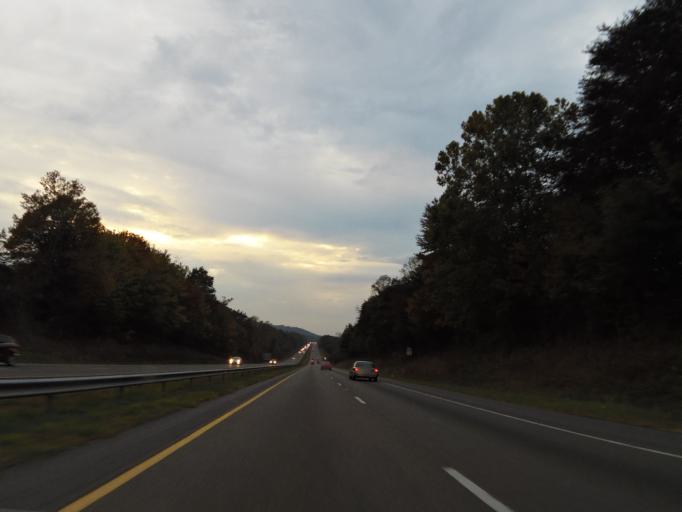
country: US
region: North Carolina
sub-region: Burke County
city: Valdese
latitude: 35.7275
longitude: -81.5659
